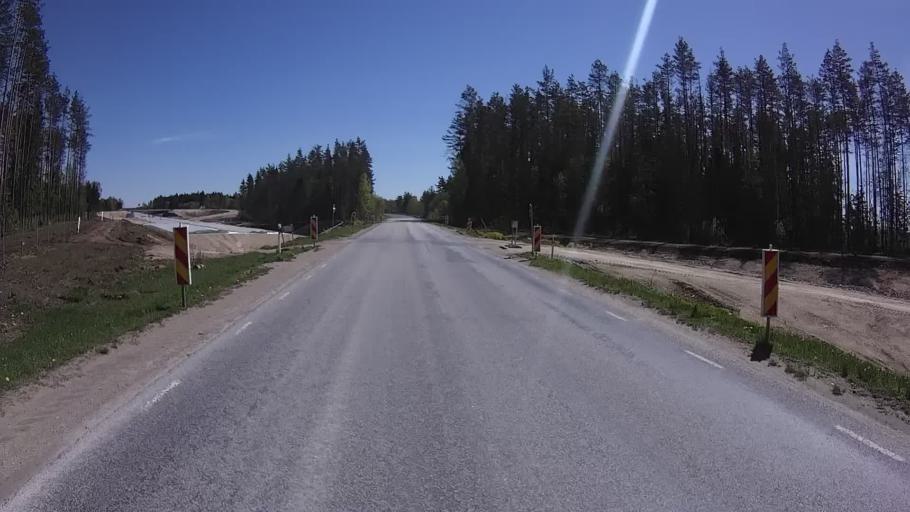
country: EE
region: Harju
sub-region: Raasiku vald
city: Raasiku
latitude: 59.1608
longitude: 25.1823
